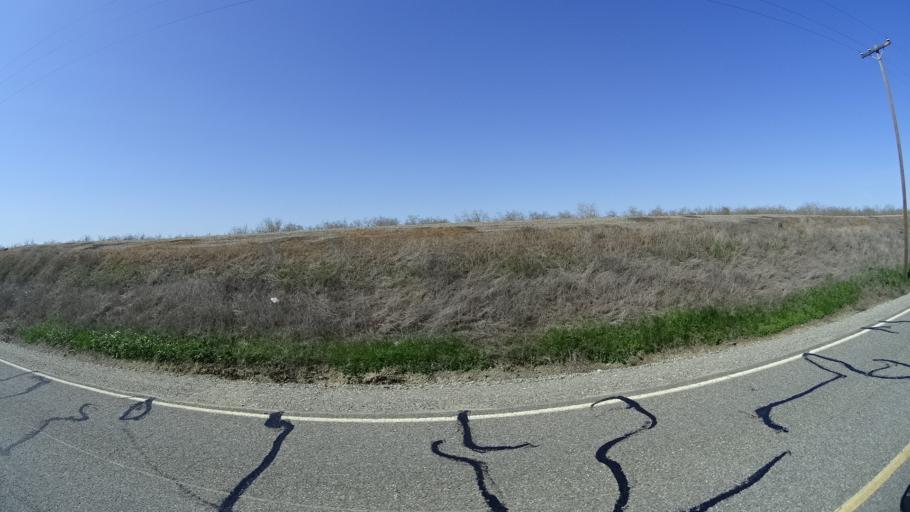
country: US
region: California
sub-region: Glenn County
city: Hamilton City
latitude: 39.7494
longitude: -122.0217
